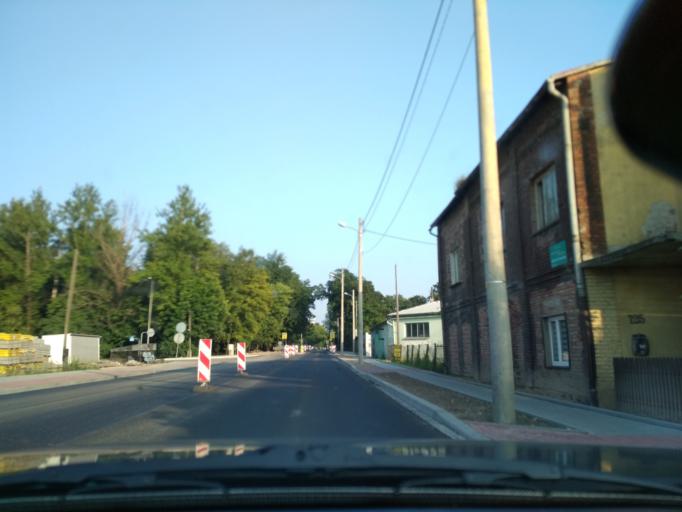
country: PL
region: Silesian Voivodeship
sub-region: Powiat zawiercianski
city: Ogrodzieniec
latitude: 50.4636
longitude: 19.4930
